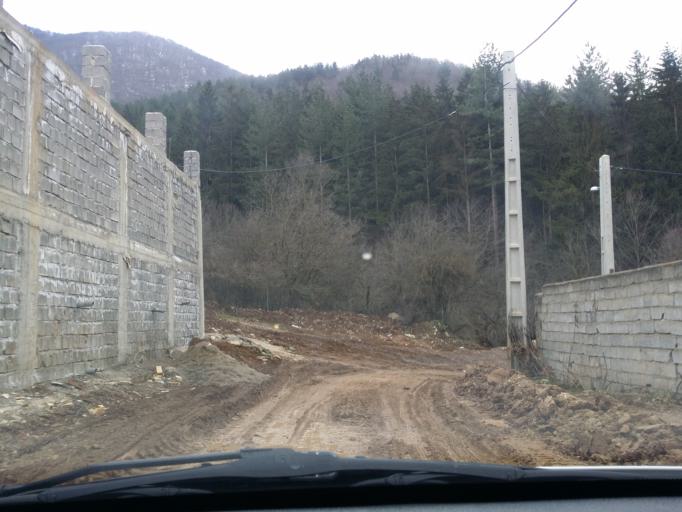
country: IR
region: Mazandaran
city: `Abbasabad
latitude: 36.4968
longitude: 51.1796
